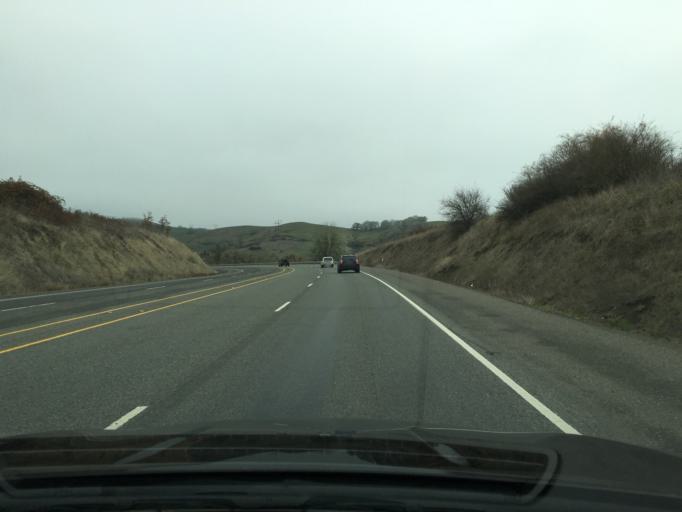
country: US
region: Oregon
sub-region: Douglas County
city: Roseburg North
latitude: 43.2112
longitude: -123.2460
